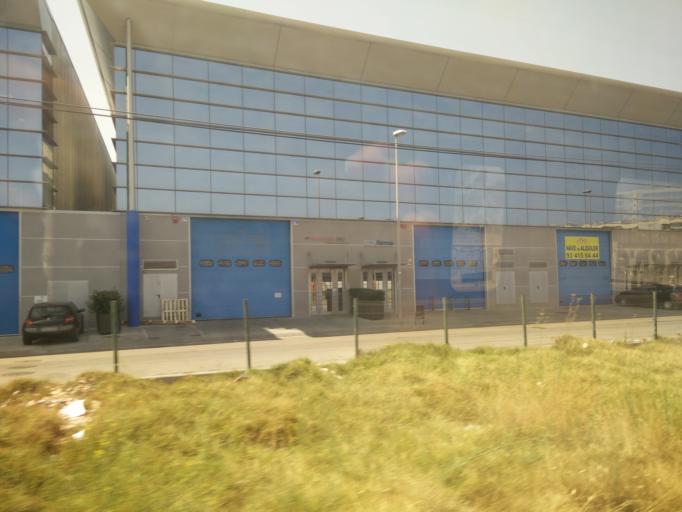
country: ES
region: Catalonia
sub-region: Provincia de Barcelona
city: Sant Adria de Besos
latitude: 41.4294
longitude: 2.2346
